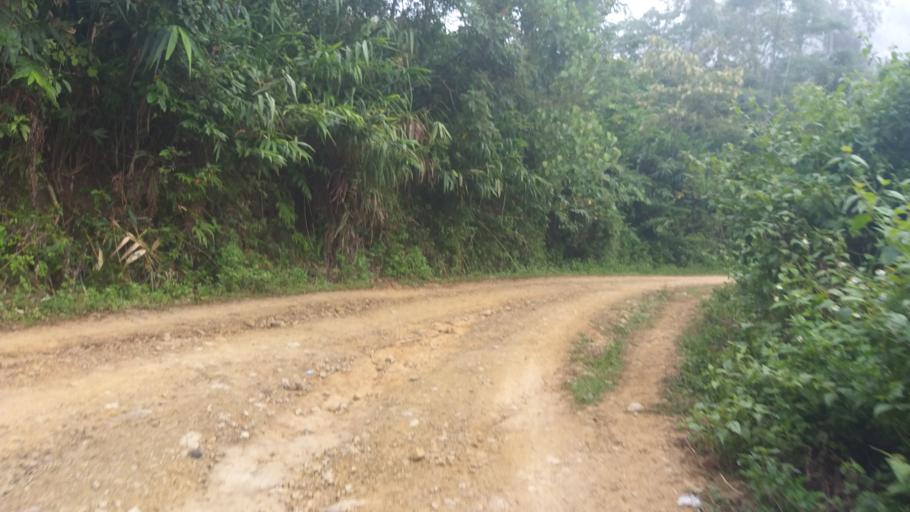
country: LA
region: Phongsali
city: Khoa
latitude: 21.2561
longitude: 102.6642
